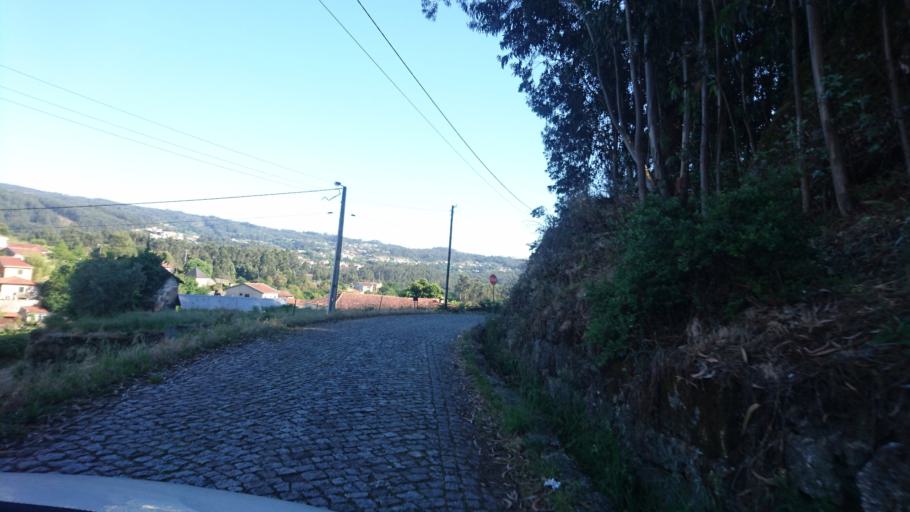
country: PT
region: Porto
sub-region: Paredes
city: Baltar
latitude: 41.1652
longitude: -8.3751
